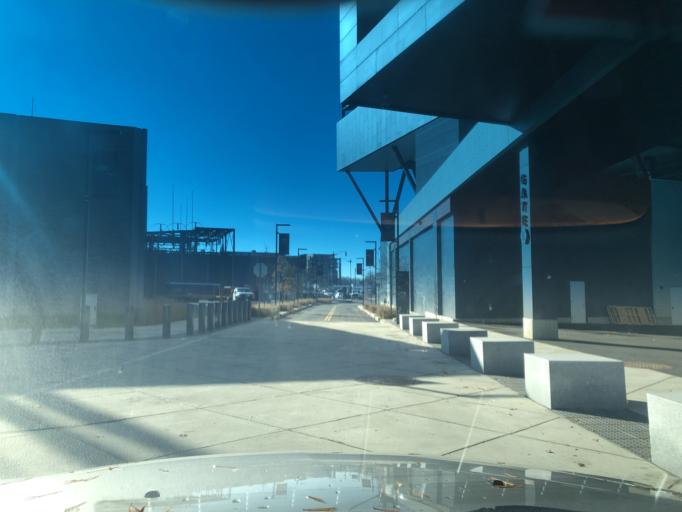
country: US
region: Washington, D.C.
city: Washington, D.C.
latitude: 38.8683
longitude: -77.0117
